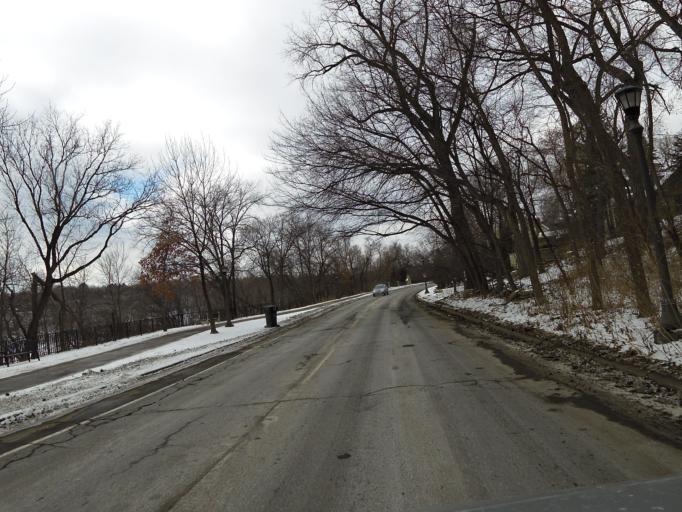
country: US
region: Minnesota
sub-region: Ramsey County
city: Lauderdale
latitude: 44.9541
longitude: -93.2061
